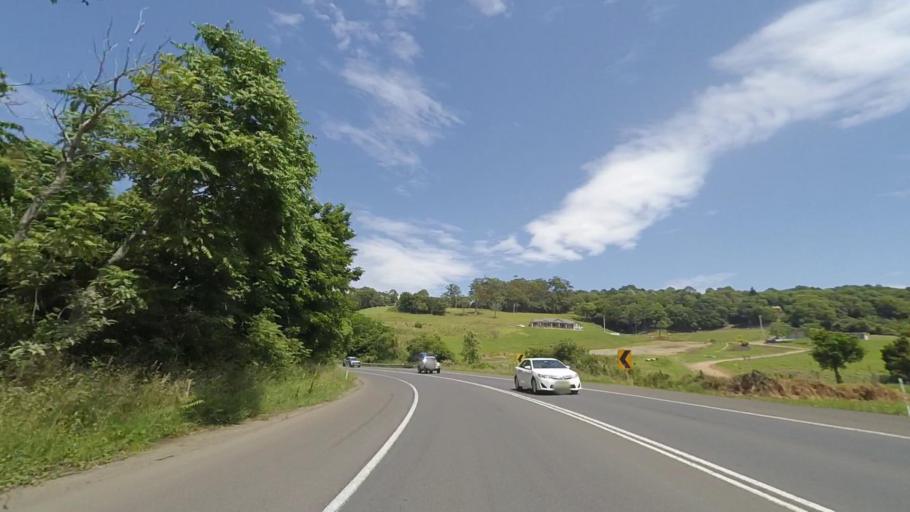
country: AU
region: New South Wales
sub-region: Shoalhaven Shire
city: Berry
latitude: -34.7481
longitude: 150.7502
